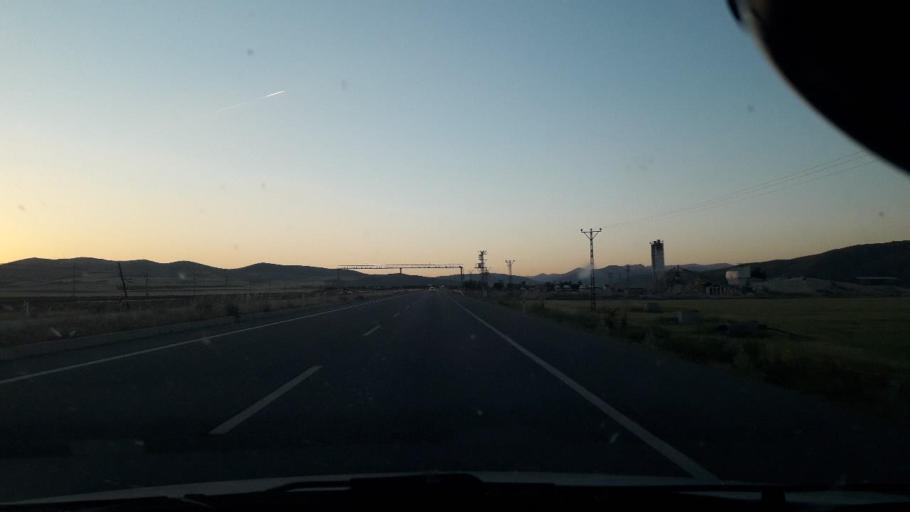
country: TR
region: Malatya
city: Yazihan
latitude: 38.6088
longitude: 38.1760
